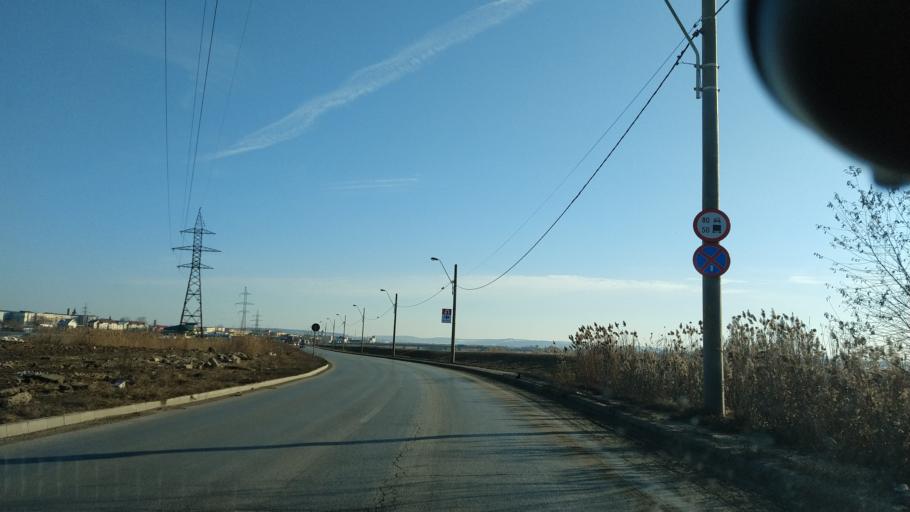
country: RO
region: Neamt
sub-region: Municipiul Roman
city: Roman
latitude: 46.9232
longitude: 26.9107
